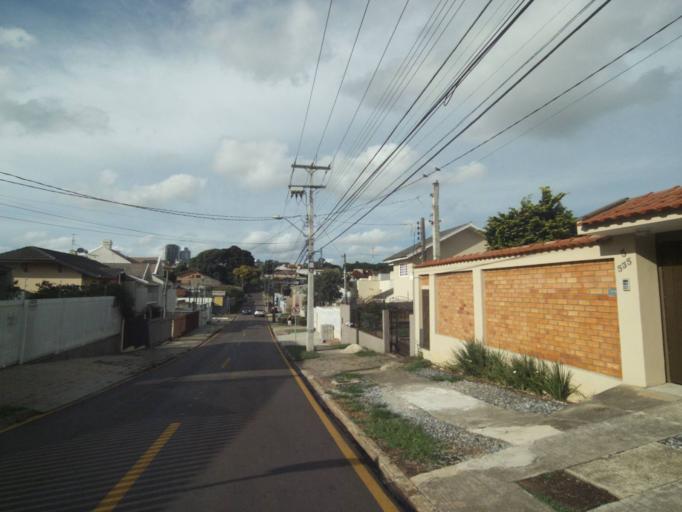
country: BR
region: Parana
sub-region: Curitiba
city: Curitiba
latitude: -25.4464
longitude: -49.3089
